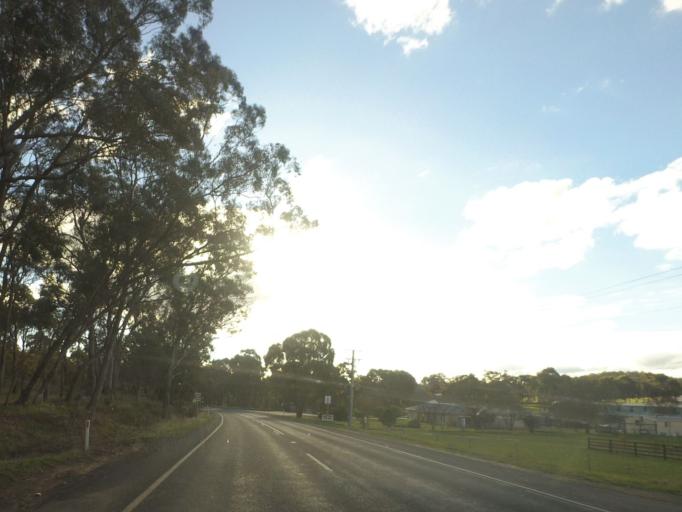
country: AU
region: Victoria
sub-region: Mount Alexander
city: Castlemaine
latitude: -37.0895
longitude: 144.2833
